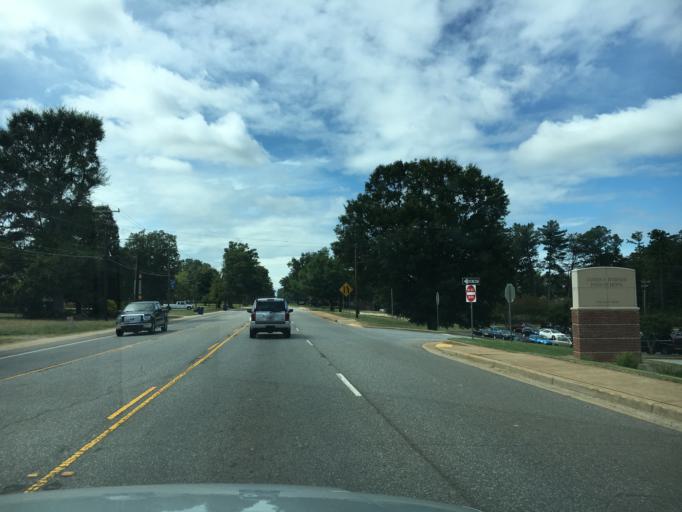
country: US
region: South Carolina
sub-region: Spartanburg County
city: Lyman
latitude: 34.9331
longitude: -82.1294
